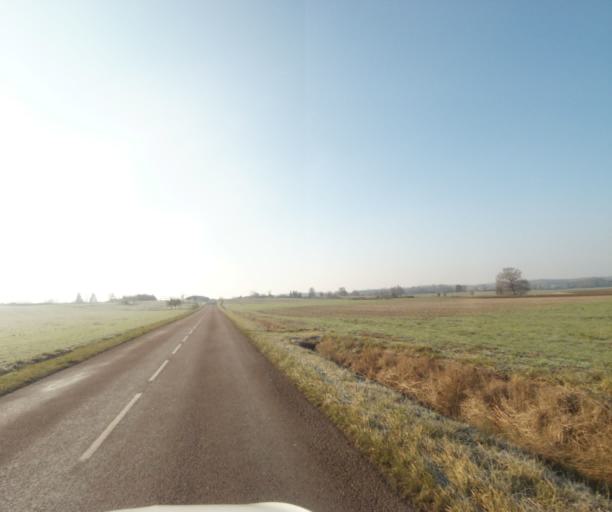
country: FR
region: Champagne-Ardenne
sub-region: Departement de la Haute-Marne
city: Montier-en-Der
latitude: 48.4172
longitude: 4.7429
